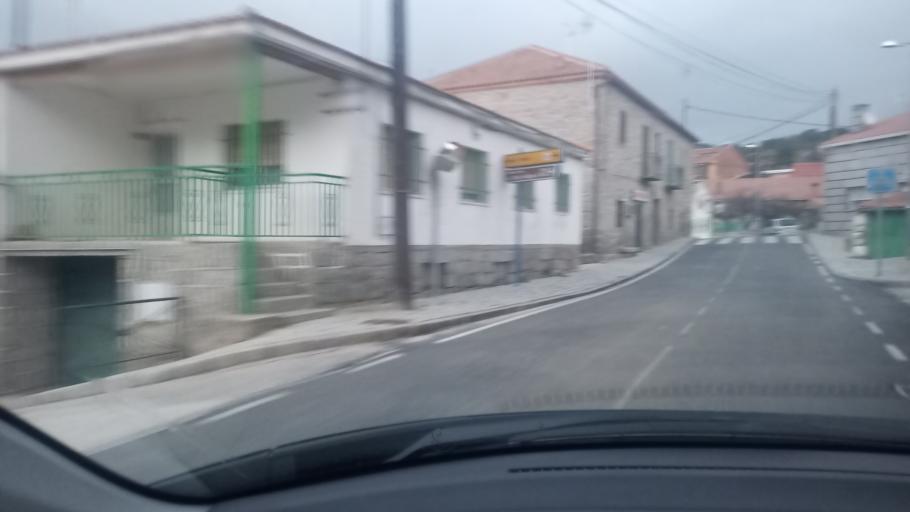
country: ES
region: Madrid
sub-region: Provincia de Madrid
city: Zarzalejo
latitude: 40.5482
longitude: -4.1826
